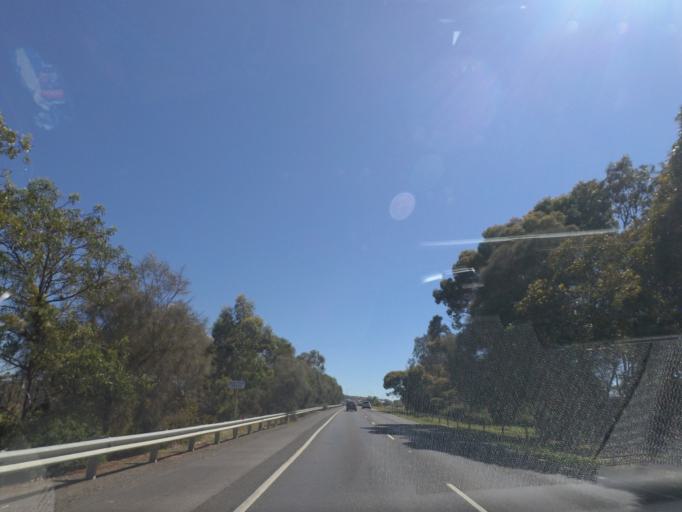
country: AU
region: Victoria
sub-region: Hume
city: Craigieburn
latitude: -37.5879
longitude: 144.9412
